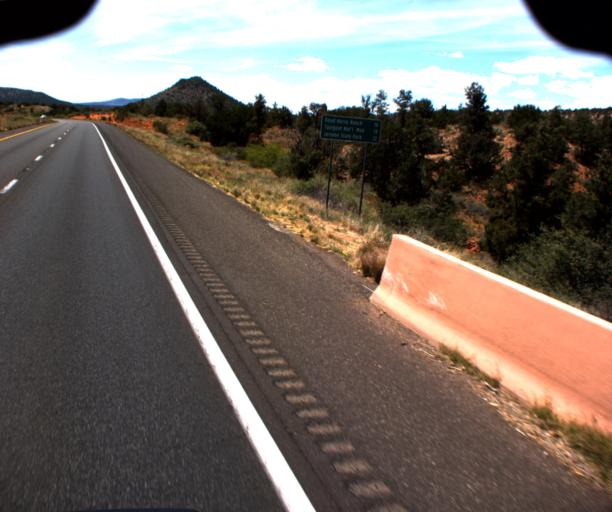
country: US
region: Arizona
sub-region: Yavapai County
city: West Sedona
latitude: 34.8454
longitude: -111.8536
